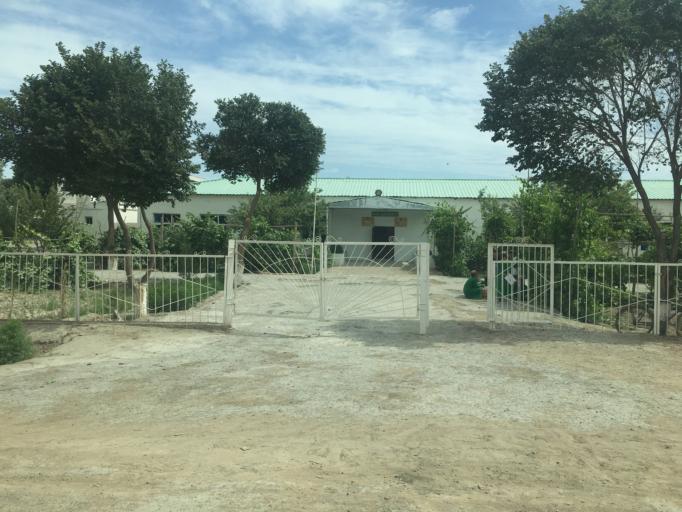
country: TM
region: Dasoguz
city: Tagta
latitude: 41.6023
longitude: 59.8463
